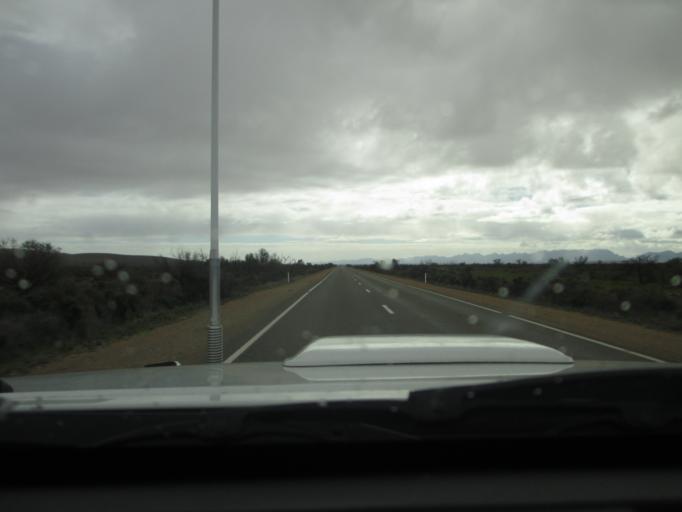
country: AU
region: South Australia
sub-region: Flinders Ranges
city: Quorn
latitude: -31.5135
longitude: 138.4279
